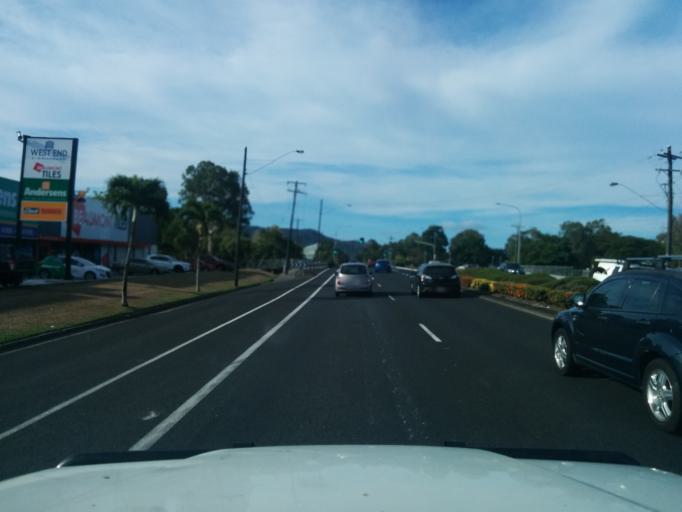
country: AU
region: Queensland
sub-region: Cairns
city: Woree
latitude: -16.9324
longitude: 145.7432
